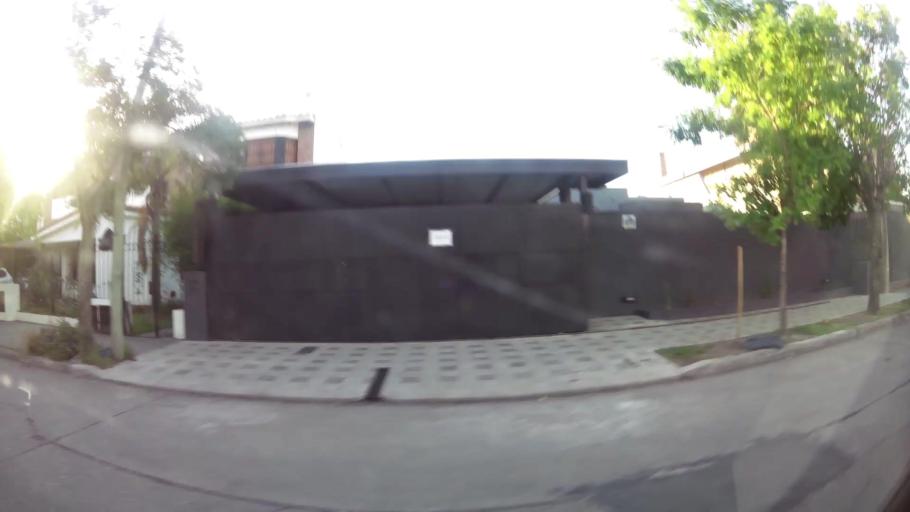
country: AR
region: Cordoba
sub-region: Departamento de Capital
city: Cordoba
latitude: -31.3780
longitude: -64.2336
